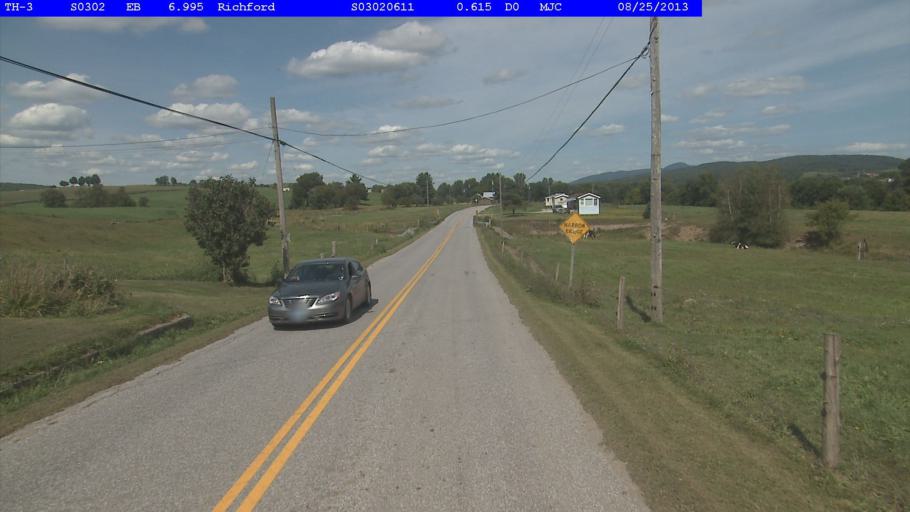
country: US
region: Vermont
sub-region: Franklin County
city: Richford
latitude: 44.9948
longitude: -72.6853
